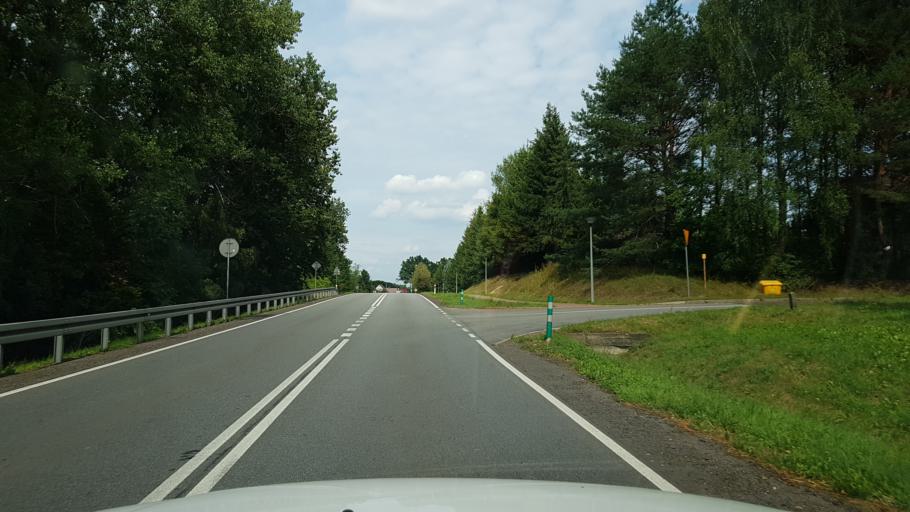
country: PL
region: West Pomeranian Voivodeship
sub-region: Powiat walecki
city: Walcz
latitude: 53.2963
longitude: 16.5269
